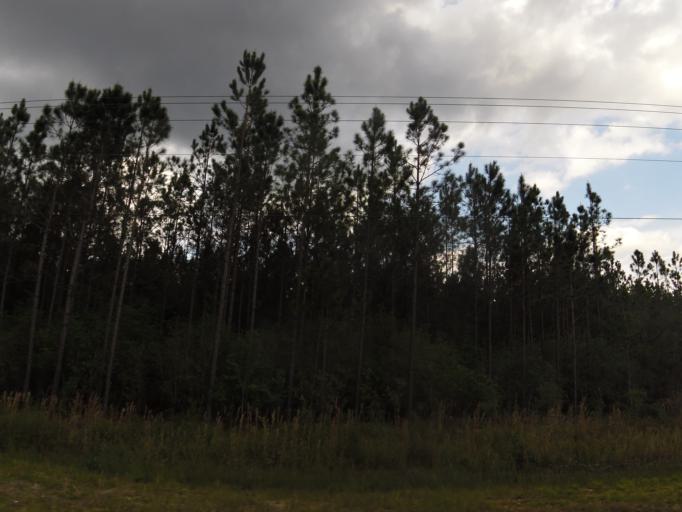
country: US
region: Georgia
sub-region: Charlton County
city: Folkston
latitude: 30.8487
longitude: -81.9536
